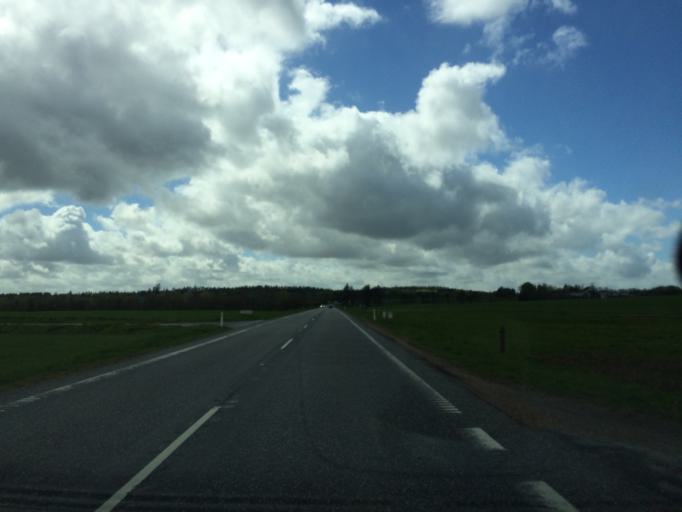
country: DK
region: Central Jutland
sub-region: Viborg Kommune
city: Stoholm
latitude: 56.4299
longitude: 9.1036
